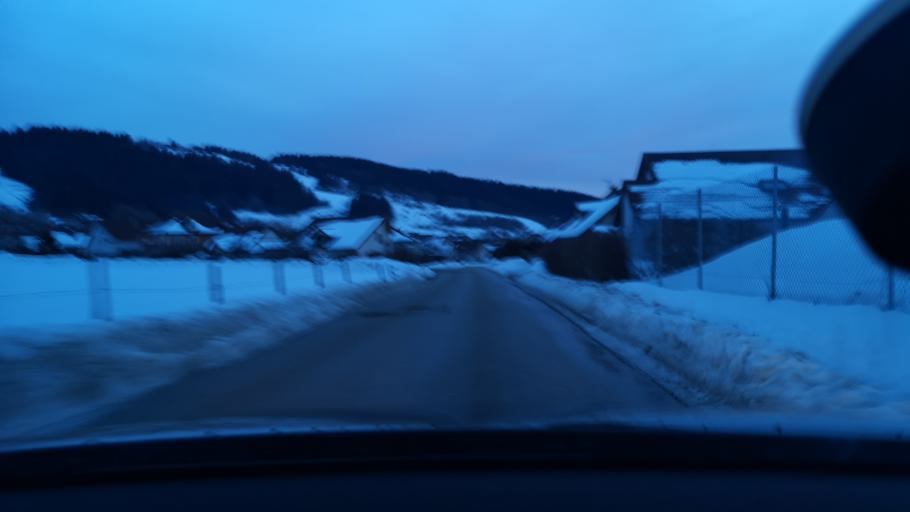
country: FR
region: Franche-Comte
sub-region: Departement du Doubs
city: Pontarlier
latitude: 46.9040
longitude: 6.3715
